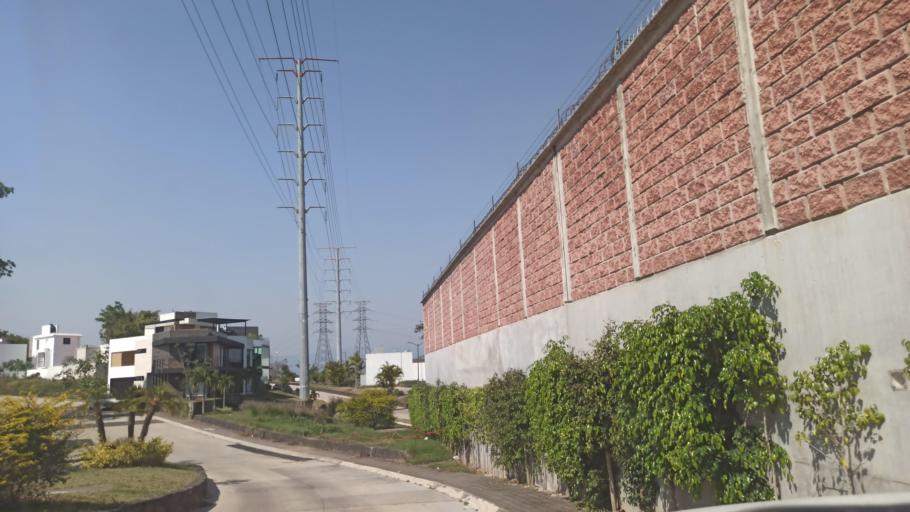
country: MX
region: Veracruz
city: El Castillo
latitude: 19.5272
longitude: -96.8639
